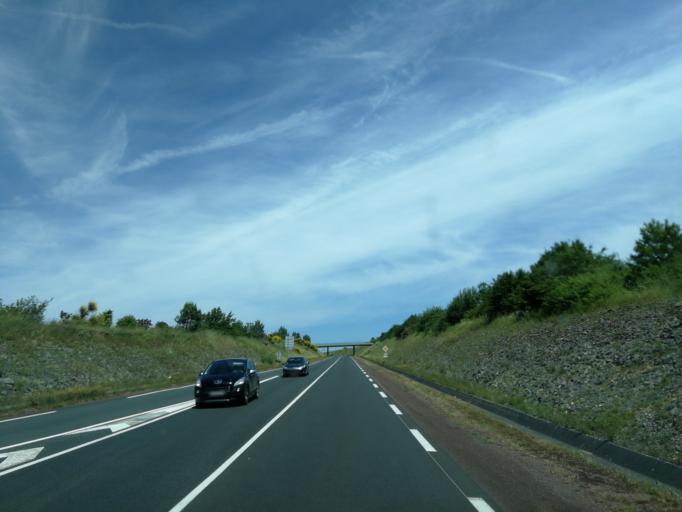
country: FR
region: Pays de la Loire
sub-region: Departement de la Vendee
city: Serigne
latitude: 46.4949
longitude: -0.8293
